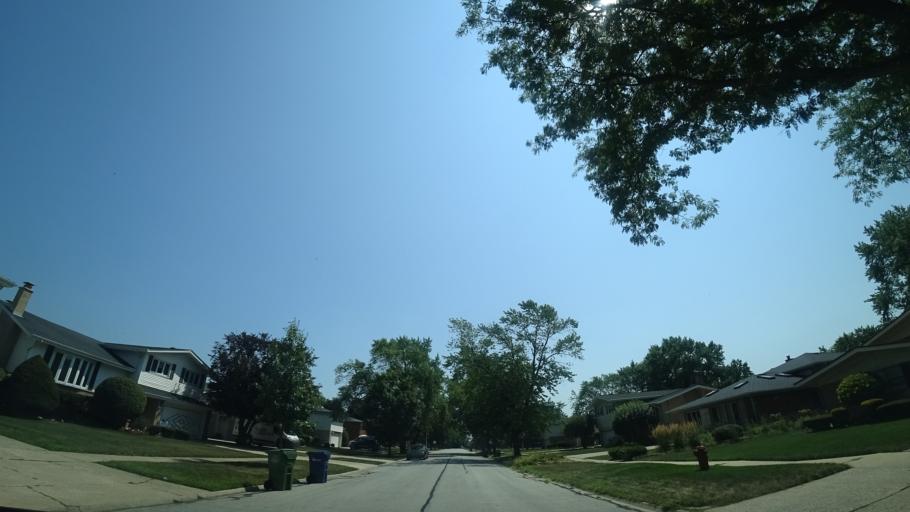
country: US
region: Illinois
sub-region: Cook County
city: Oak Lawn
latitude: 41.7026
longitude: -87.7548
